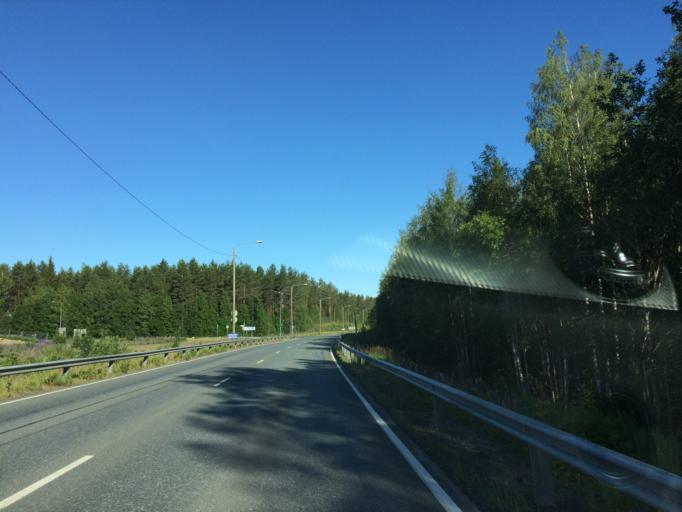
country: FI
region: Haeme
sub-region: Haemeenlinna
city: Haemeenlinna
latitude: 60.9601
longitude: 24.4587
